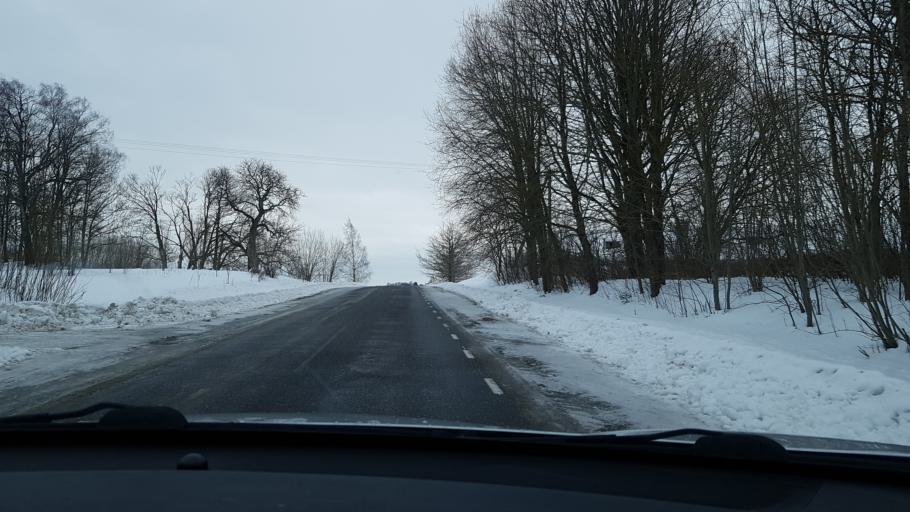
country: EE
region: Jaervamaa
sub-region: Koeru vald
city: Koeru
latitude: 58.9821
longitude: 25.9905
